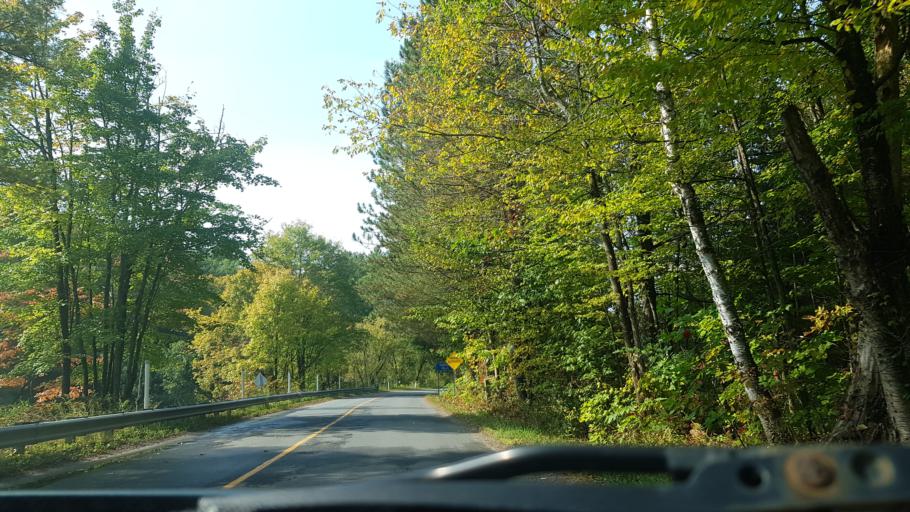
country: CA
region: Ontario
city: Gravenhurst
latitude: 44.7900
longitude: -79.2263
